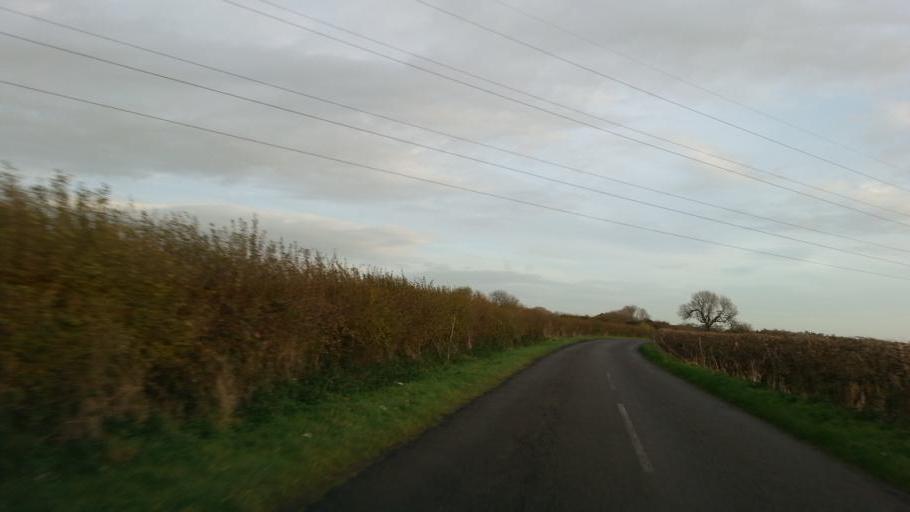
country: GB
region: England
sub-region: Nottinghamshire
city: Farndon
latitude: 53.0042
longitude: -0.8326
